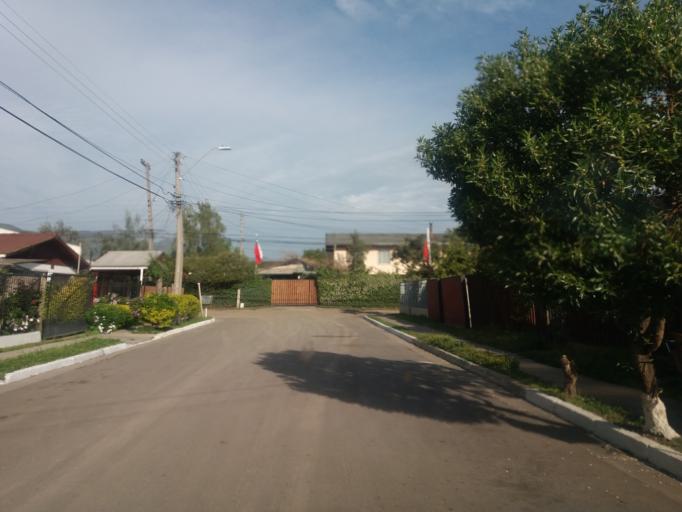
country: CL
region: Valparaiso
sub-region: Provincia de Quillota
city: Hacienda La Calera
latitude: -32.7842
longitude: -71.1764
